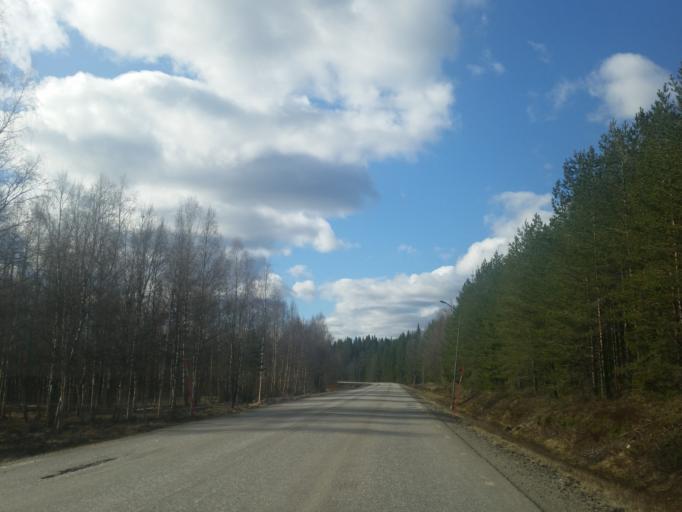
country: SE
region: Vaesterbotten
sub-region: Robertsfors Kommun
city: Robertsfors
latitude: 64.1994
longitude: 20.8334
